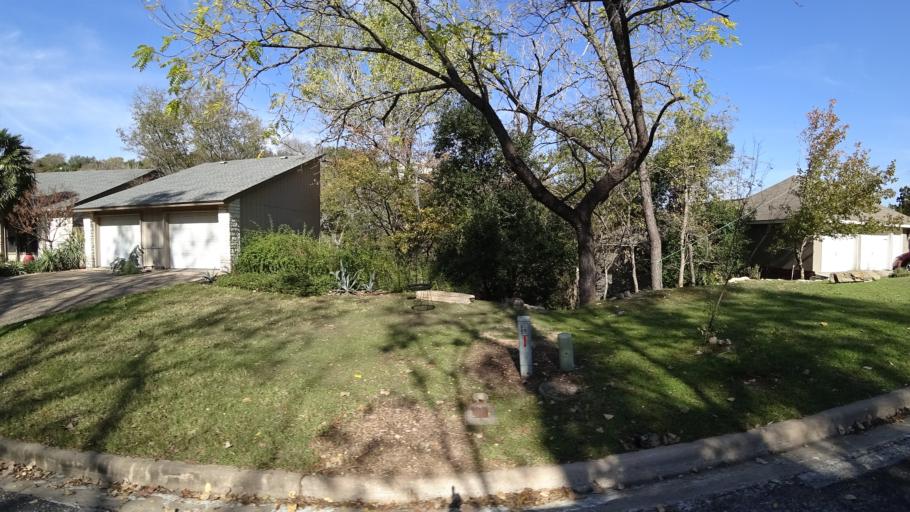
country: US
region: Texas
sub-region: Williamson County
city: Jollyville
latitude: 30.3716
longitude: -97.7709
